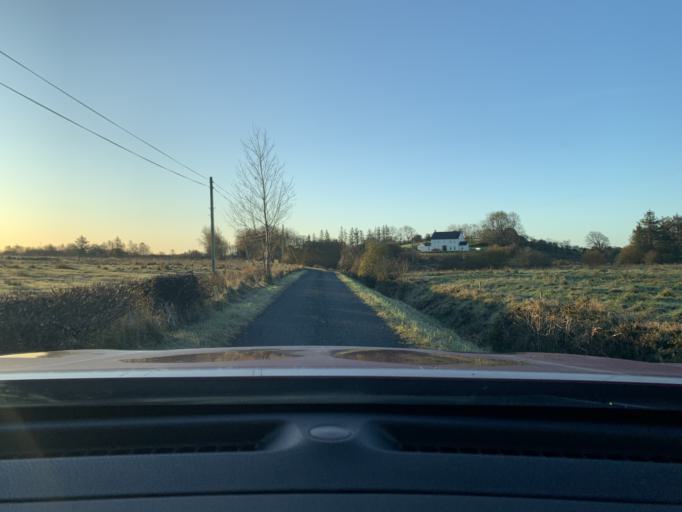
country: IE
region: Connaught
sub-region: Sligo
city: Ballymote
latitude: 54.0843
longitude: -8.5486
